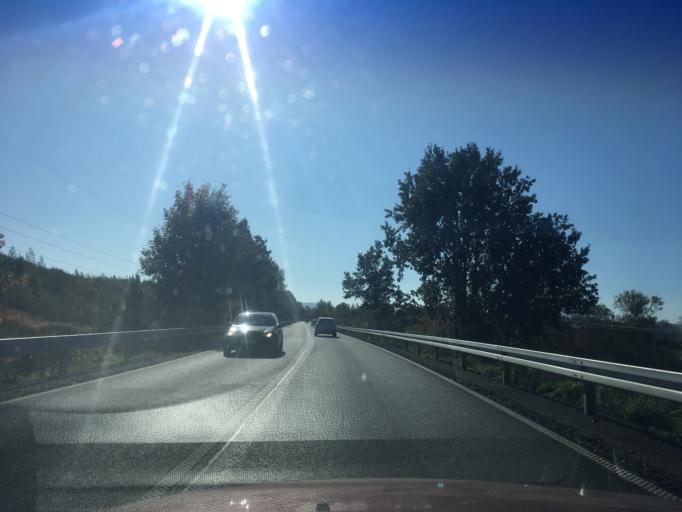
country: DE
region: Saxony
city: Hirschfelde
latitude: 50.9244
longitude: 14.8728
